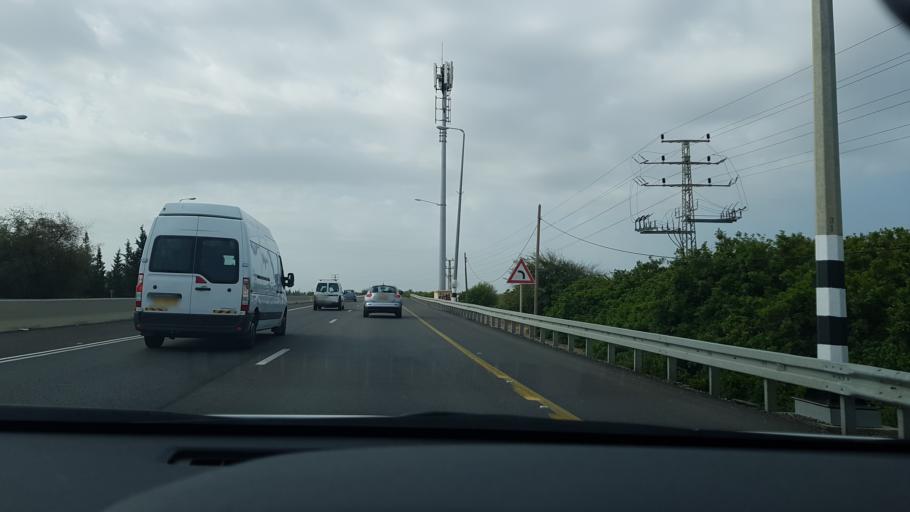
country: IL
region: Southern District
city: Ashqelon
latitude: 31.6462
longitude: 34.5934
